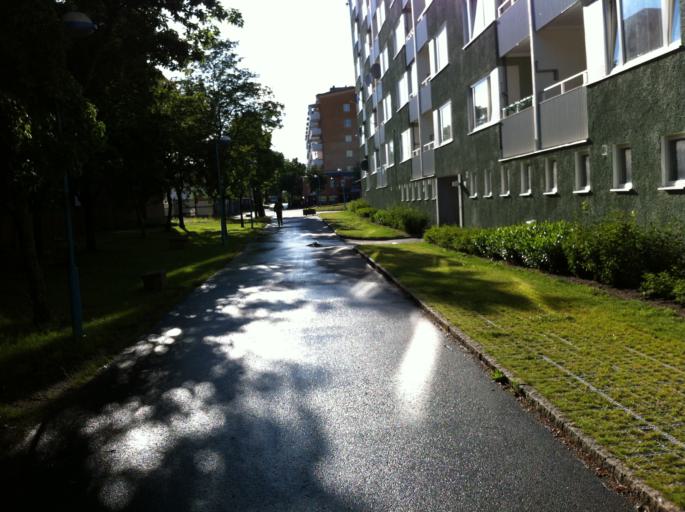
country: SE
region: Stockholm
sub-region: Stockholms Kommun
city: Kista
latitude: 59.3899
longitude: 17.9298
